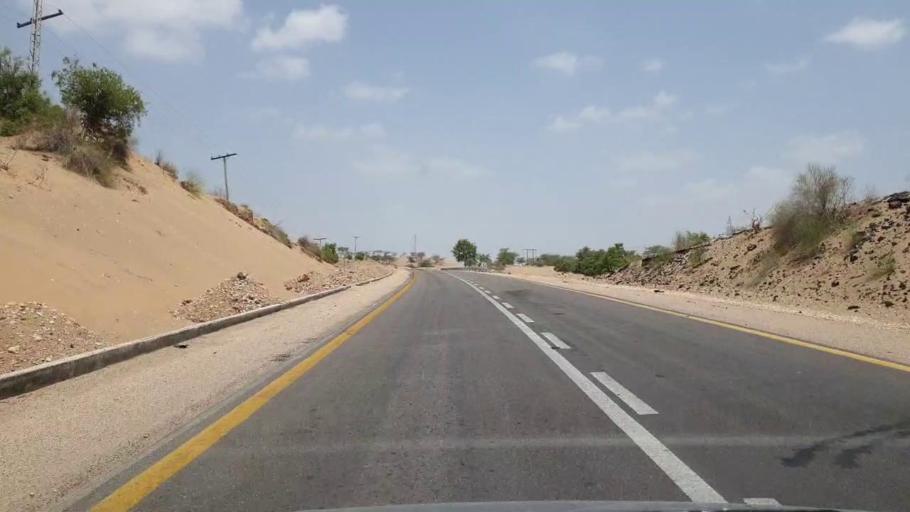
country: PK
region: Sindh
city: Mithi
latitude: 24.8150
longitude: 69.7057
